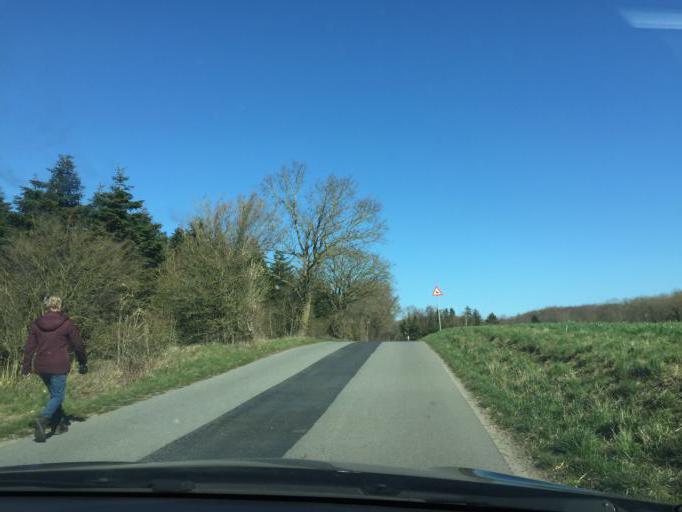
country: DK
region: South Denmark
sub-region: Kerteminde Kommune
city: Langeskov
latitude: 55.3431
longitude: 10.5695
